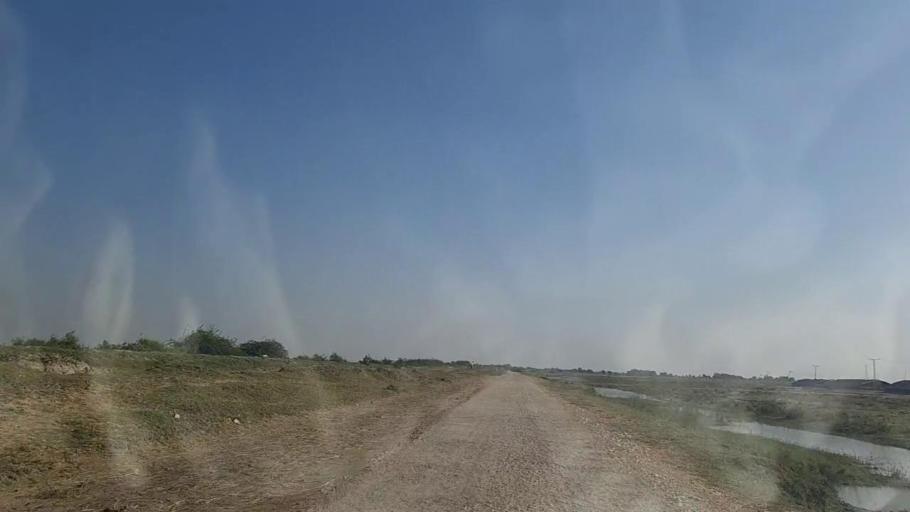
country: PK
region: Sindh
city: Mirpur Batoro
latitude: 24.6103
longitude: 68.1692
